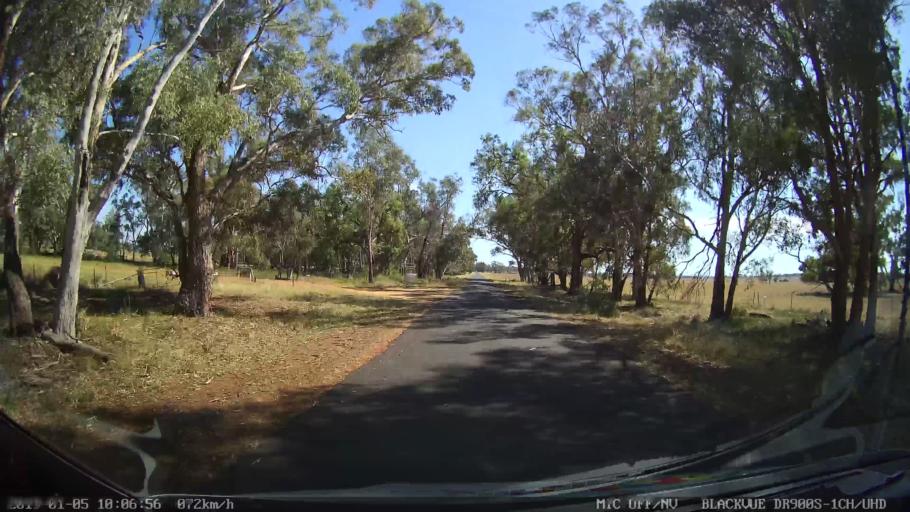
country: AU
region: New South Wales
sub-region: Gilgandra
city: Gilgandra
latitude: -31.6535
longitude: 148.8718
